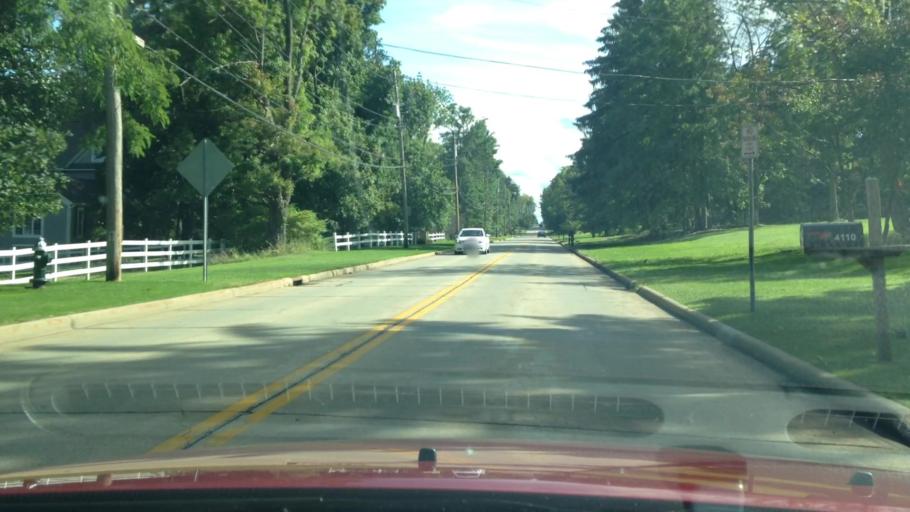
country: US
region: Ohio
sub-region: Cuyahoga County
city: Orange
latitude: 41.4481
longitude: -81.4635
